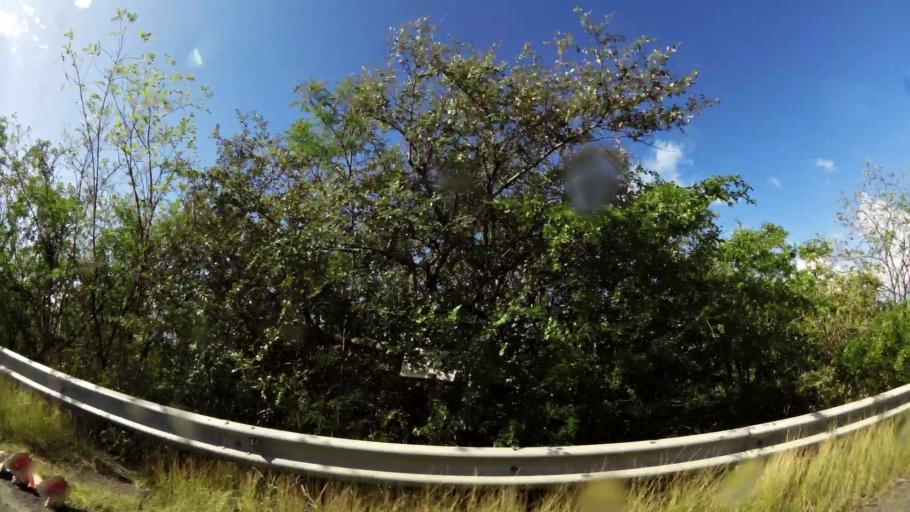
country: MQ
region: Martinique
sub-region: Martinique
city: Les Trois-Ilets
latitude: 14.4594
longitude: -61.0655
